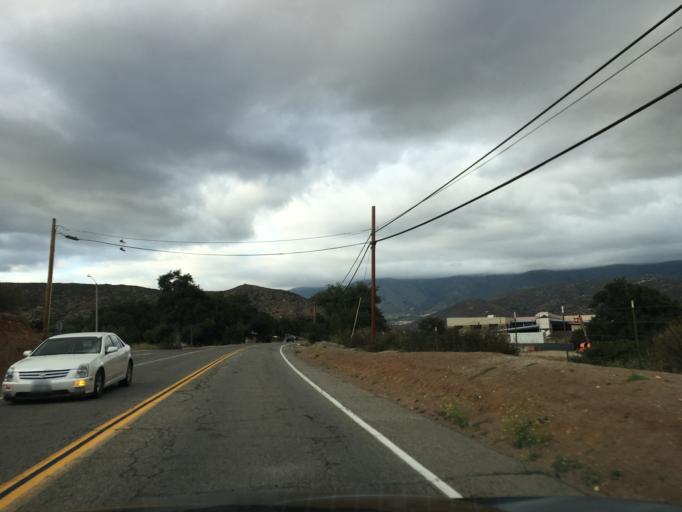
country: US
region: California
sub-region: San Diego County
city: Valley Center
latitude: 33.2499
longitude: -116.9632
